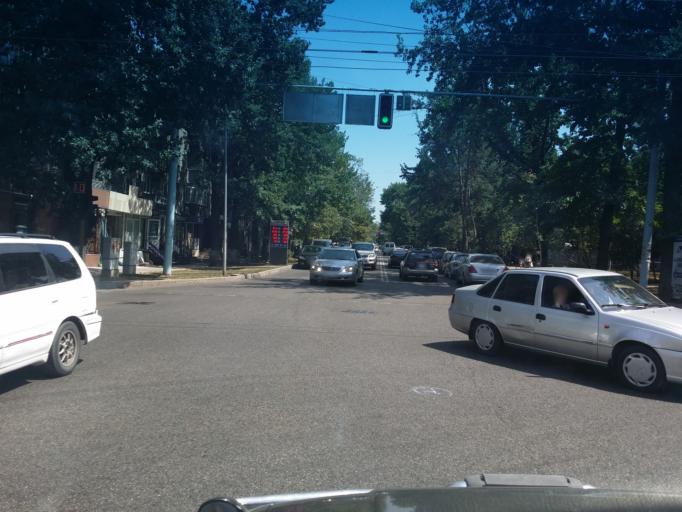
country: KZ
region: Almaty Qalasy
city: Almaty
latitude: 43.2557
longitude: 76.9324
